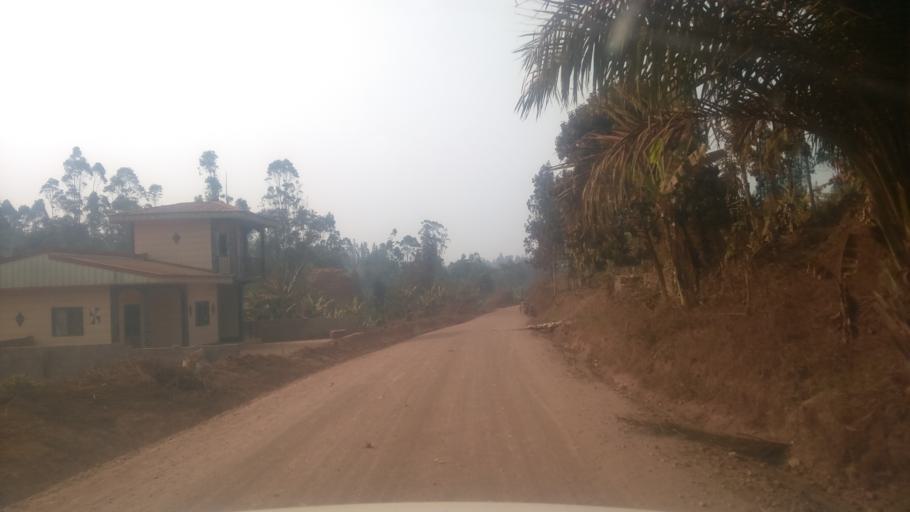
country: CM
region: West
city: Dschang
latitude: 5.4803
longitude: 10.1074
